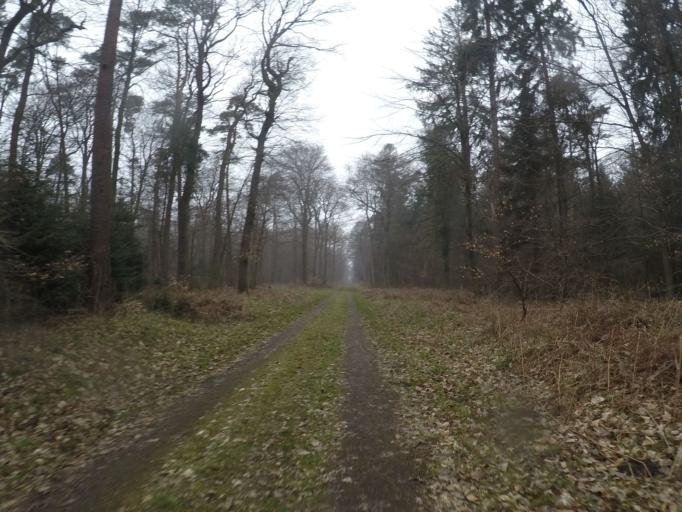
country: DE
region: Lower Saxony
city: Elmlohe
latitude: 53.6229
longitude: 8.6995
